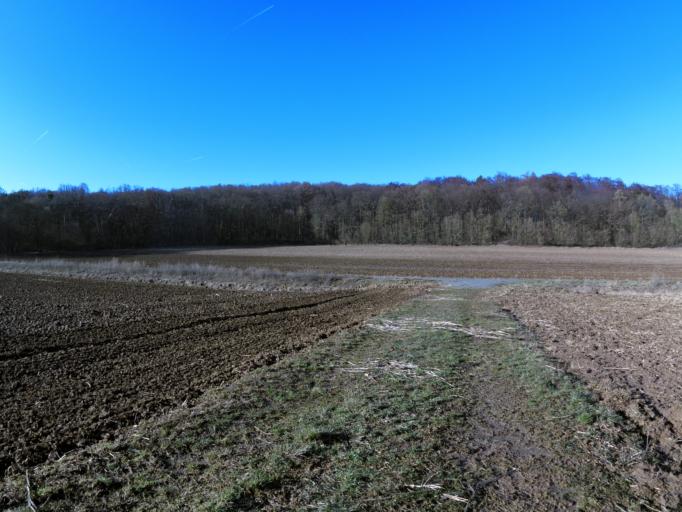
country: DE
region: Bavaria
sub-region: Regierungsbezirk Unterfranken
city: Estenfeld
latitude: 49.8496
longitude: 9.9938
